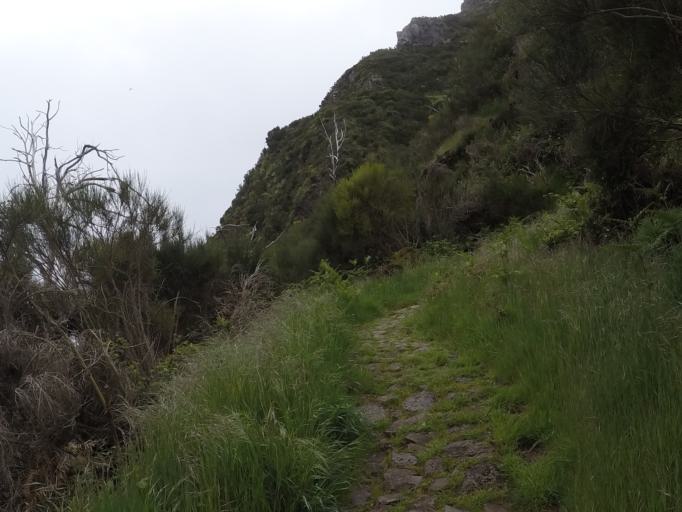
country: PT
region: Madeira
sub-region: Camara de Lobos
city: Curral das Freiras
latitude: 32.7171
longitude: -16.9897
